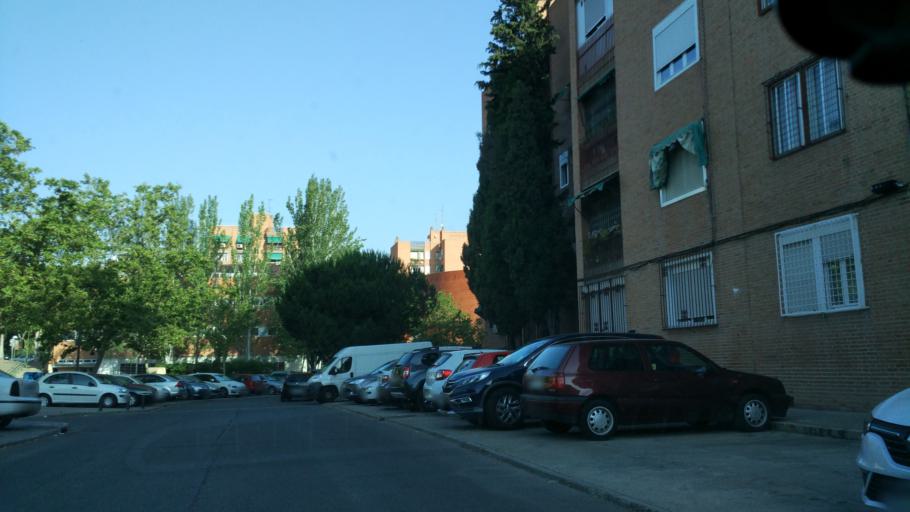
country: ES
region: Madrid
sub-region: Provincia de Madrid
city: Tetuan de las Victorias
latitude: 40.4669
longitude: -3.7183
